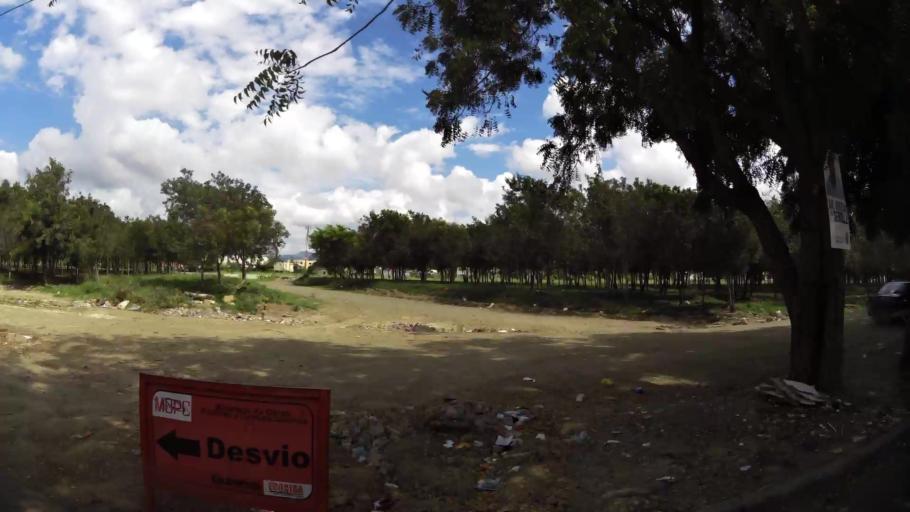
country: DO
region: Santiago
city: Santiago de los Caballeros
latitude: 19.4695
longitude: -70.7018
